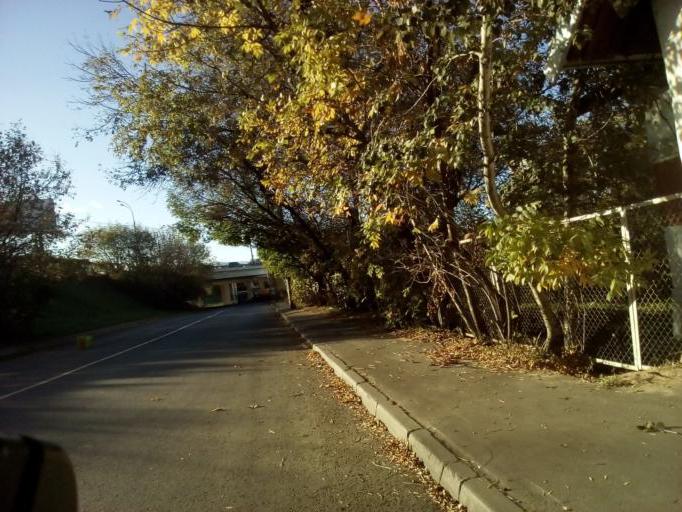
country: RU
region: Moskovskaya
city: Koptevo
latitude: 55.8405
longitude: 37.5255
